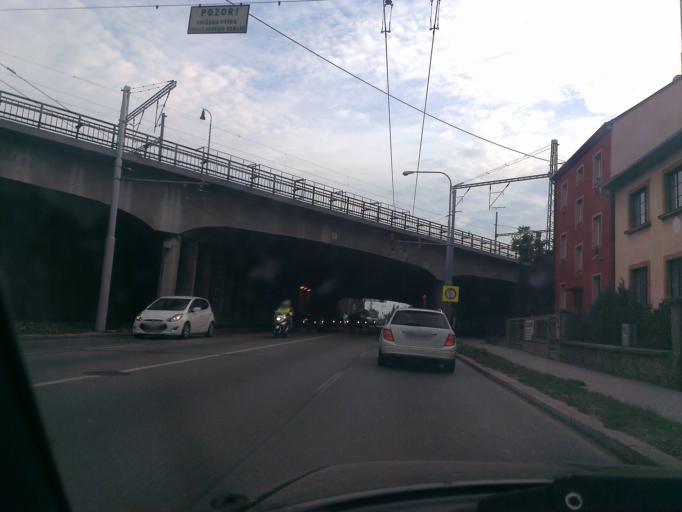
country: CZ
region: South Moravian
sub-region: Mesto Brno
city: Brno
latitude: 49.2111
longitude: 16.6430
